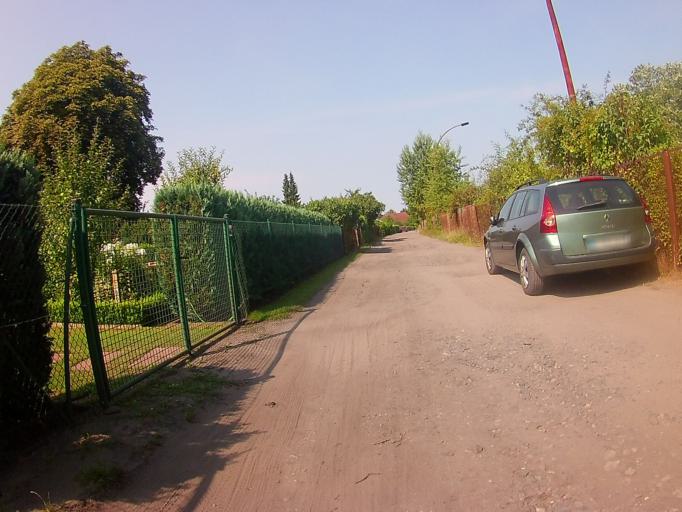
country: DE
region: Berlin
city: Adlershof
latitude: 52.4247
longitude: 13.5495
